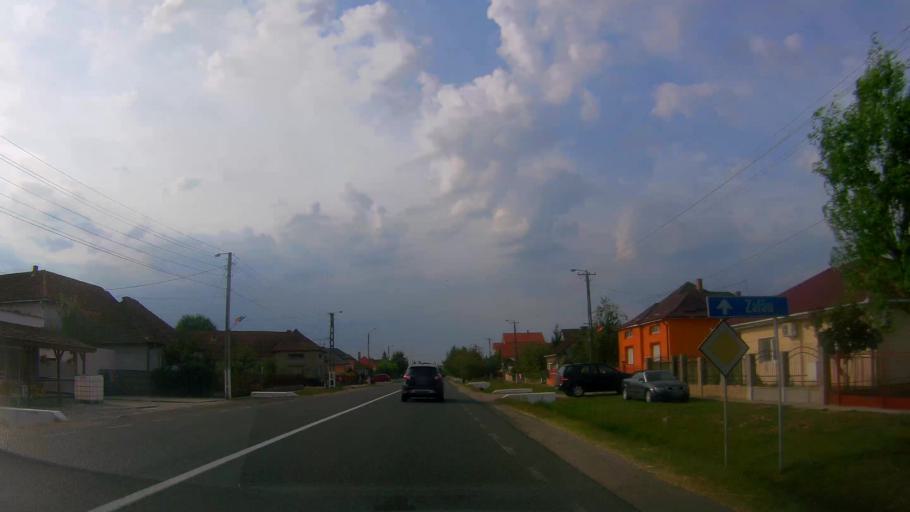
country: RO
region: Satu Mare
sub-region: Oras Ardud
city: Ardud
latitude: 47.6496
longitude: 22.8913
